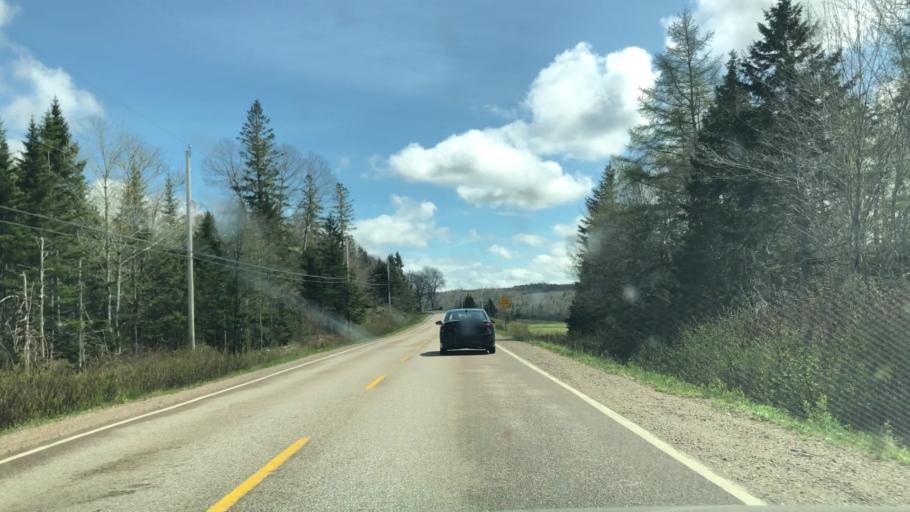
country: CA
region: Nova Scotia
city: Antigonish
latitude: 45.2041
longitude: -62.0036
